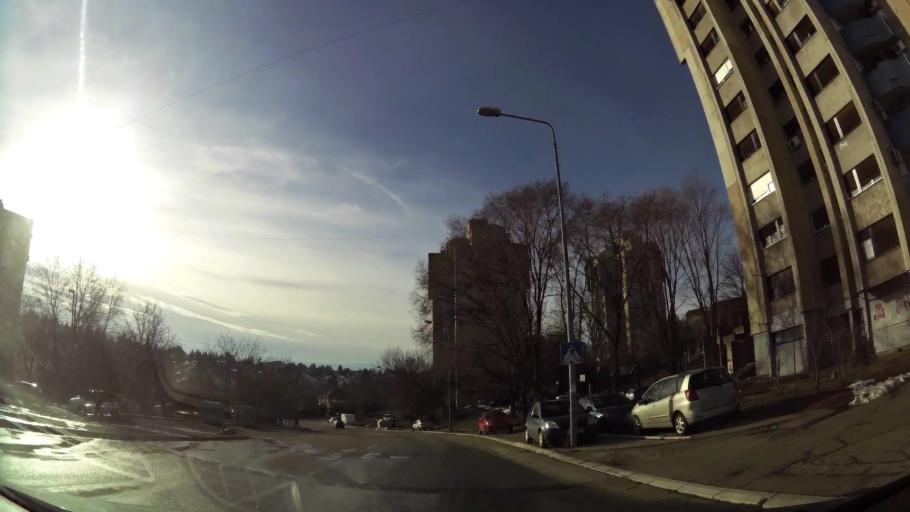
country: RS
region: Central Serbia
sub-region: Belgrade
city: Rakovica
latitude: 44.7228
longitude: 20.4303
